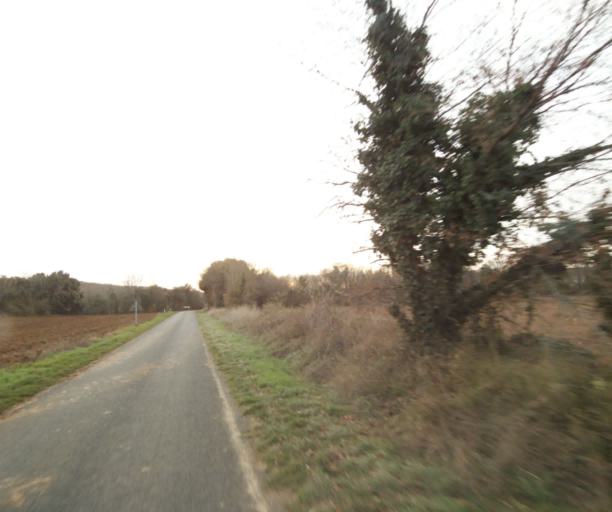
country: FR
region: Poitou-Charentes
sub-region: Departement de la Charente-Maritime
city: Fontcouverte
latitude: 45.8146
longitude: -0.5962
